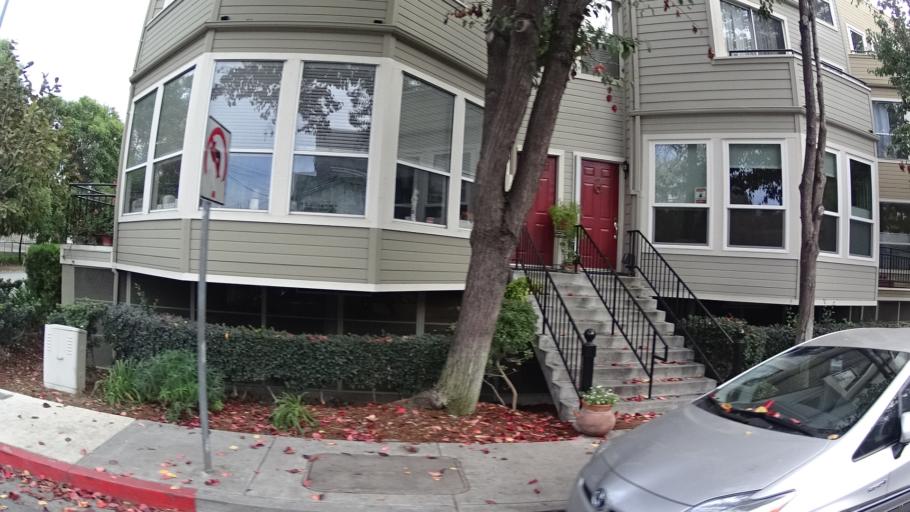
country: US
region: California
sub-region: Santa Clara County
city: San Jose
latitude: 37.3294
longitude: -121.8973
